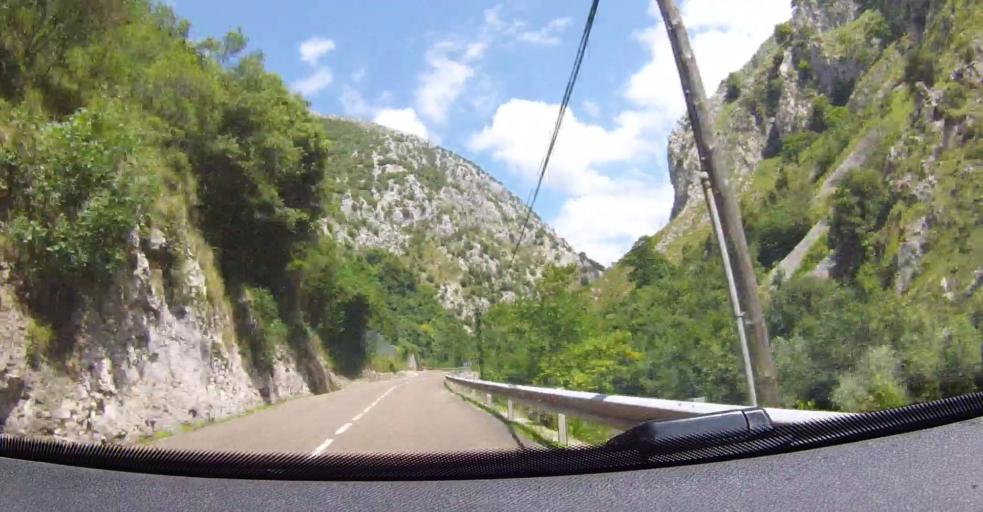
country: ES
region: Cantabria
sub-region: Provincia de Cantabria
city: Tresviso
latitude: 43.2855
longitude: -4.6260
